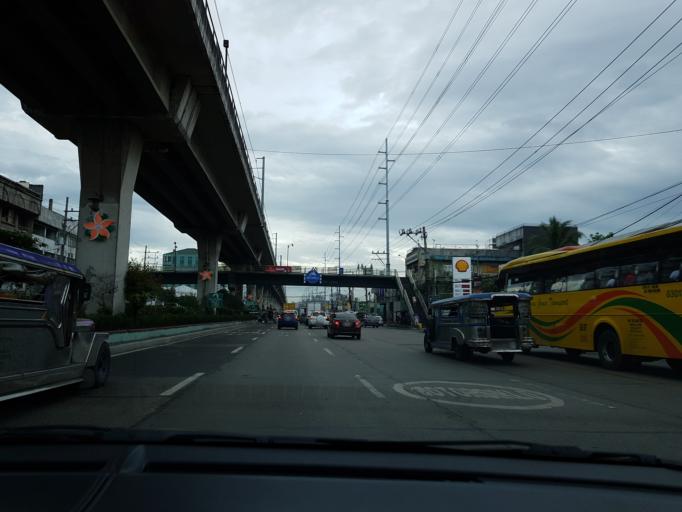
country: PH
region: Calabarzon
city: Del Monte
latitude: 14.6571
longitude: 120.9888
